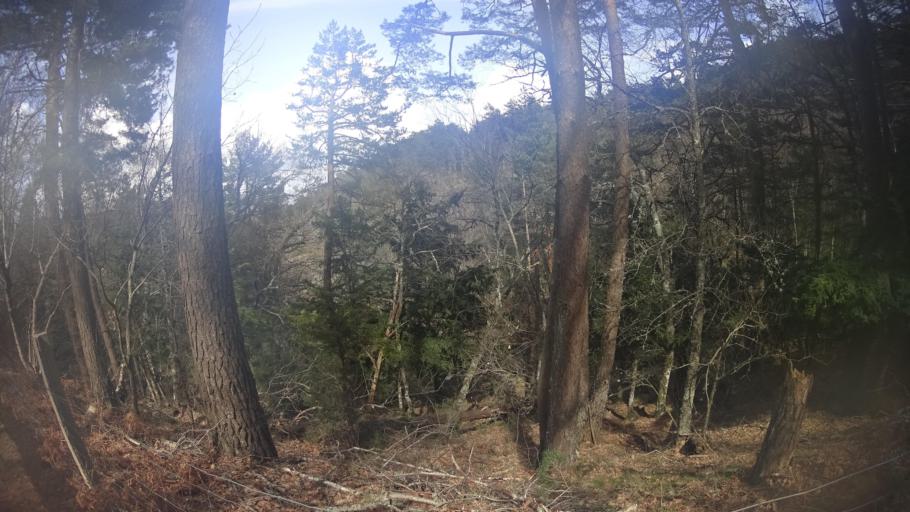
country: ES
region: Madrid
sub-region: Provincia de Madrid
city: Canencia
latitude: 40.8747
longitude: -3.7787
